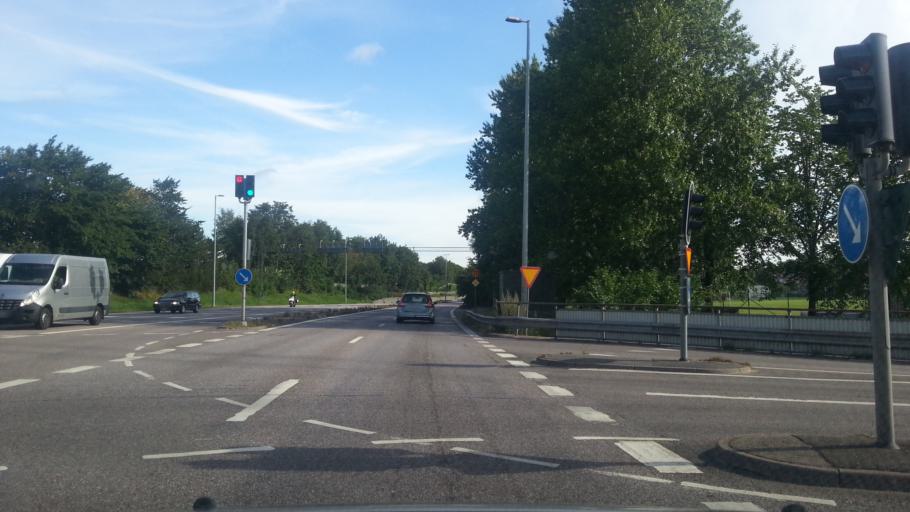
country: SE
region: Vaestra Goetaland
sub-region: Trollhattan
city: Trollhattan
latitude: 58.2894
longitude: 12.3087
